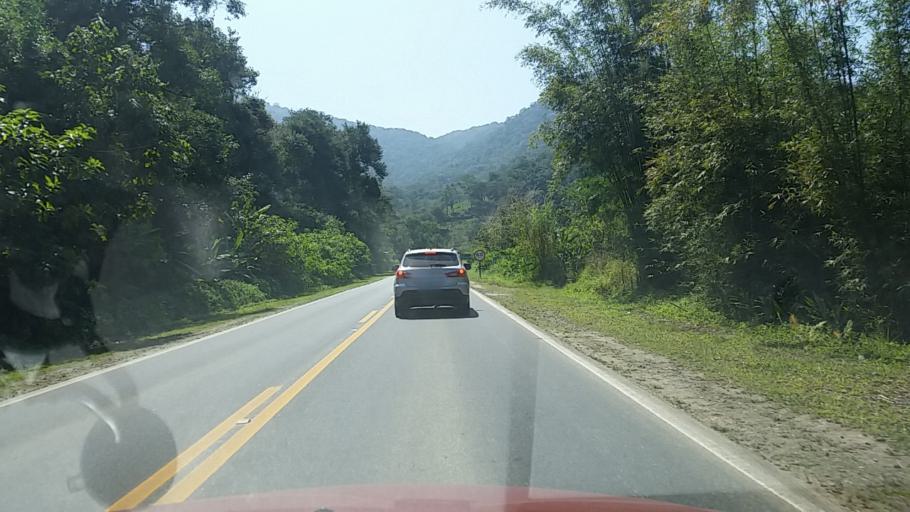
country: BR
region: Sao Paulo
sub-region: Miracatu
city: Miracatu
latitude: -24.3809
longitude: -47.5215
